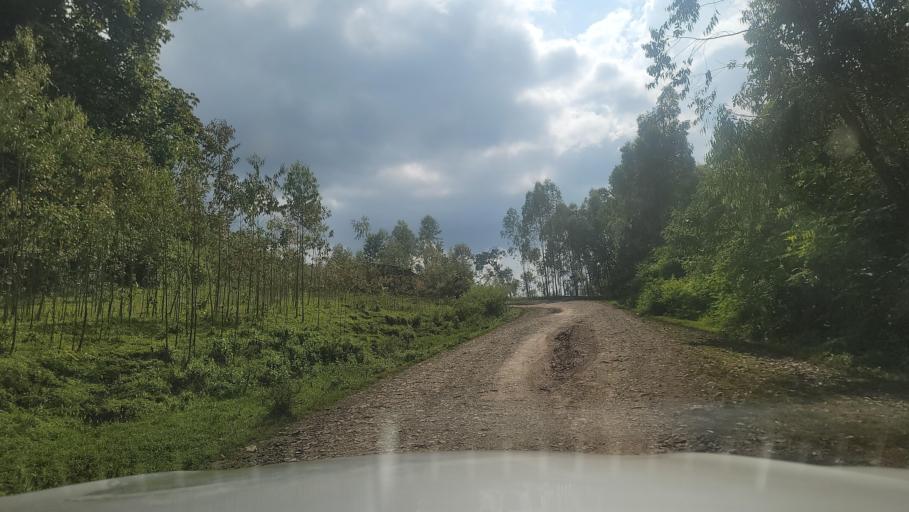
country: ET
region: Oromiya
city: Agaro
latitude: 7.7222
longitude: 36.2589
